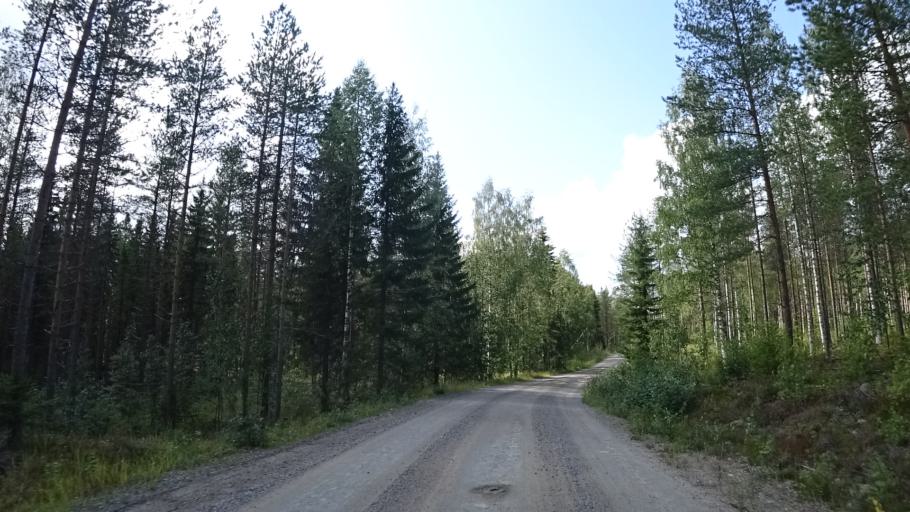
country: FI
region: North Karelia
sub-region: Joensuu
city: Ilomantsi
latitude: 62.9295
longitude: 31.3199
